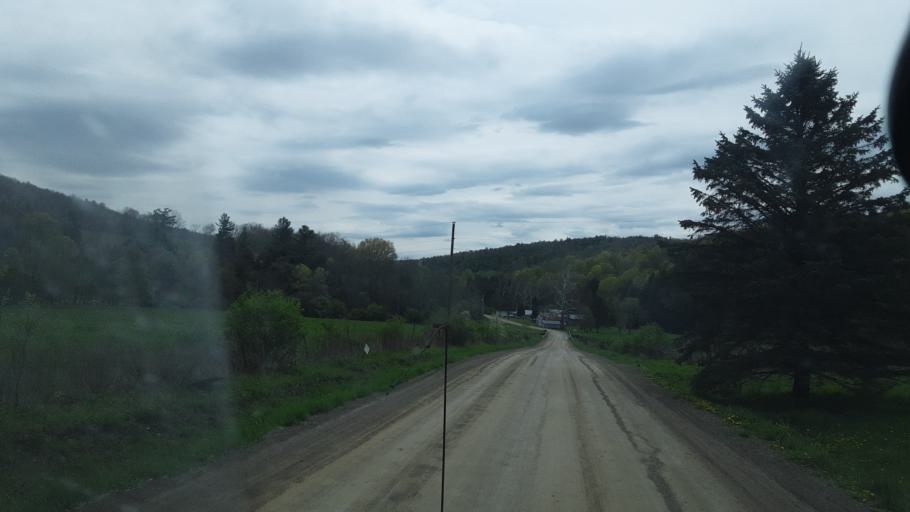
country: US
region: New York
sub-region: Steuben County
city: Addison
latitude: 42.1009
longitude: -77.3374
